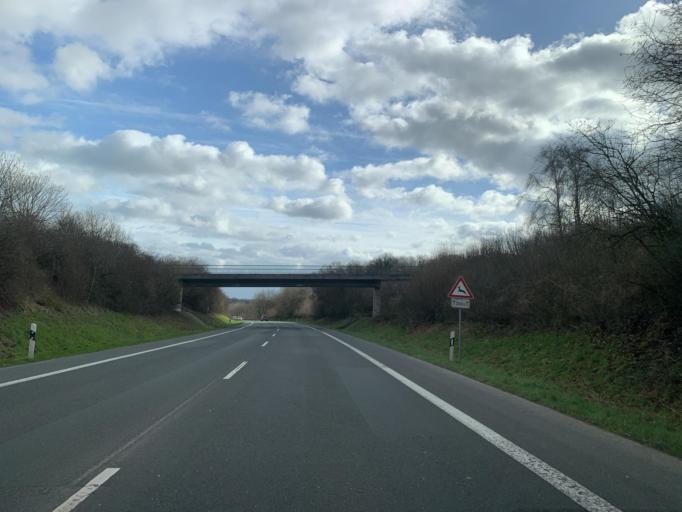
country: DE
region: North Rhine-Westphalia
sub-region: Regierungsbezirk Munster
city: Horstmar
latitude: 52.0759
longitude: 7.2976
